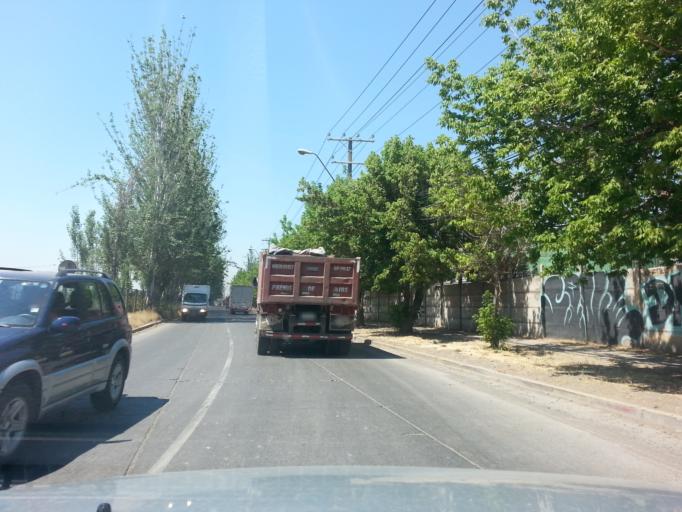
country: CL
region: Santiago Metropolitan
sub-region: Provincia de Chacabuco
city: Chicureo Abajo
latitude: -33.3538
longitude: -70.6930
